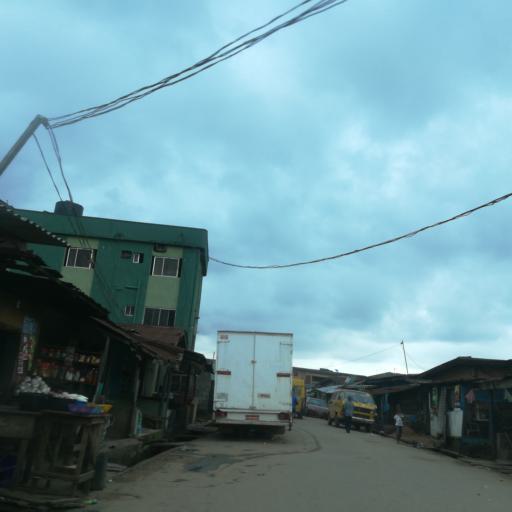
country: NG
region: Lagos
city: Agege
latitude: 6.6105
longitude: 3.2957
